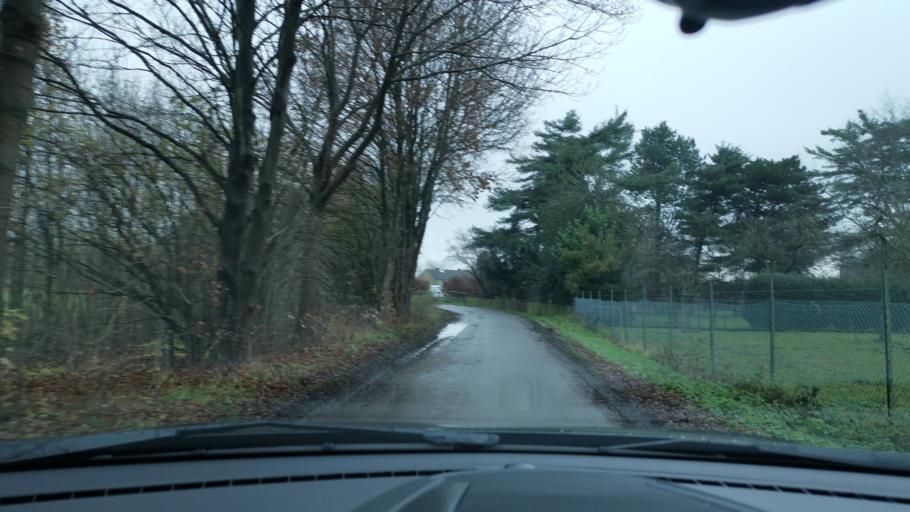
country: DE
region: North Rhine-Westphalia
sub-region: Regierungsbezirk Dusseldorf
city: Juchen
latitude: 51.1083
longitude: 6.5215
